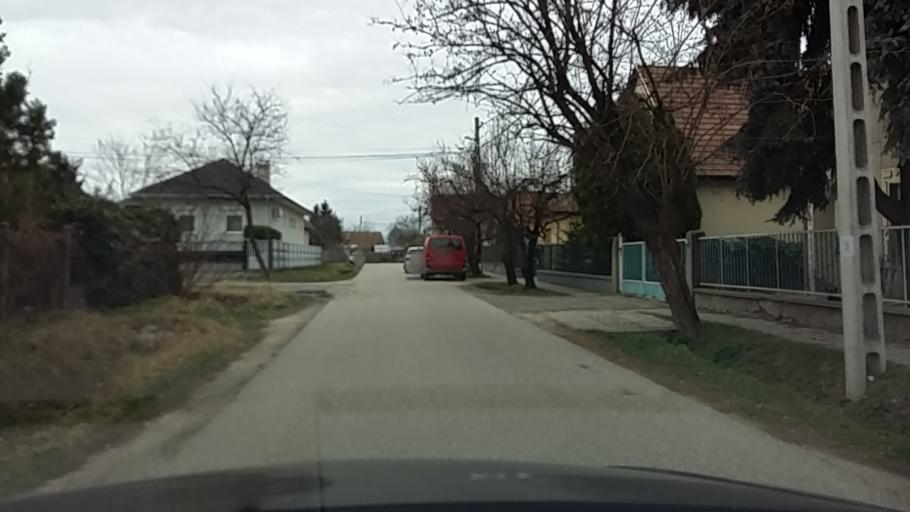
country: HU
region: Pest
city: Szigetszentmiklos
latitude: 47.3553
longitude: 19.0315
